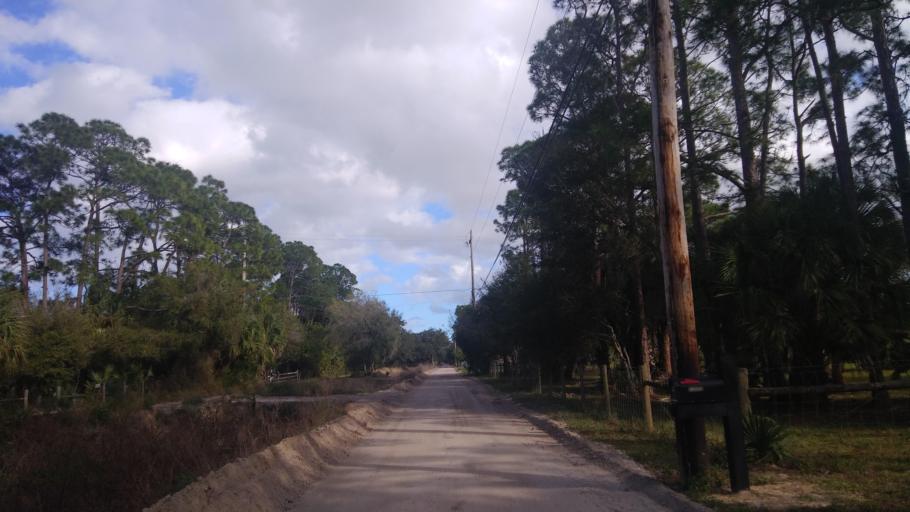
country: US
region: Florida
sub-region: Indian River County
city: Fellsmere
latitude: 27.7572
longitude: -80.5834
